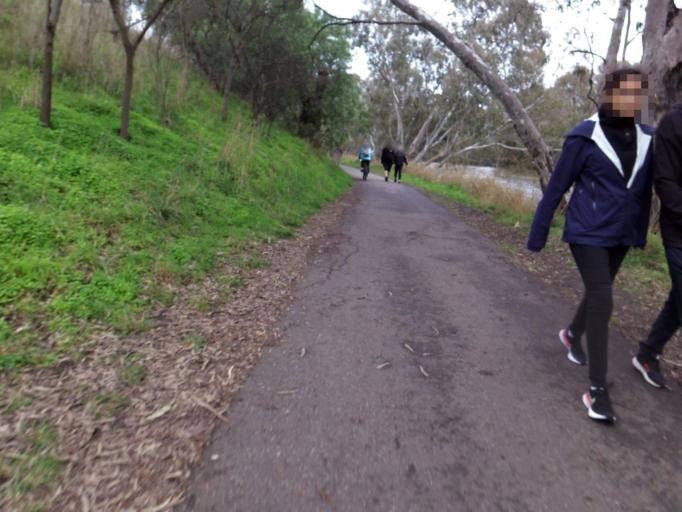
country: AU
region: Victoria
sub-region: Greater Geelong
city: Hamlyn Heights
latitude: -38.1460
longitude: 144.3228
